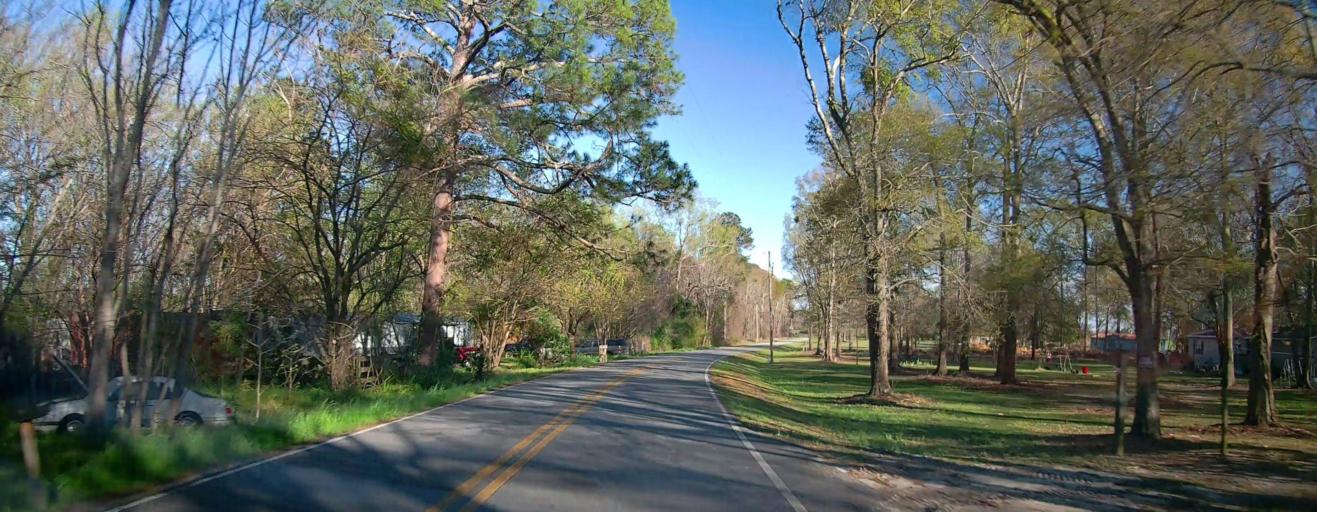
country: US
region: Georgia
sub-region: Houston County
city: Perry
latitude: 32.3636
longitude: -83.6572
